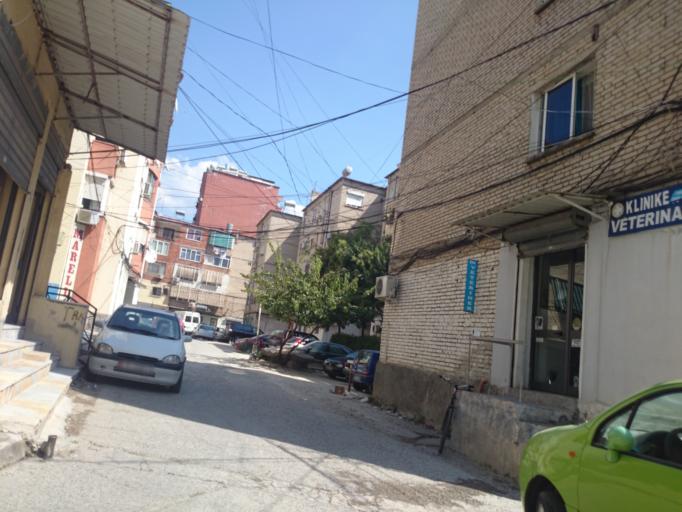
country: AL
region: Tirane
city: Tirana
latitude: 41.3252
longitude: 19.8294
